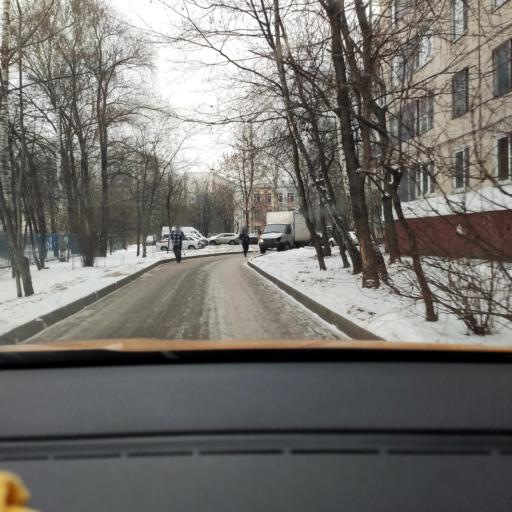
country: RU
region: Moscow
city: Bibirevo
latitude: 55.8916
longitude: 37.6033
